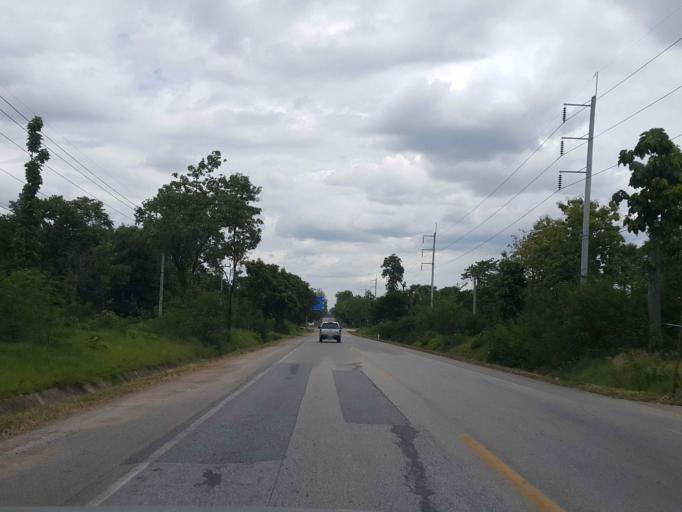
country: TH
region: Chiang Mai
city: Doi Lo
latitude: 18.4213
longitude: 98.8575
